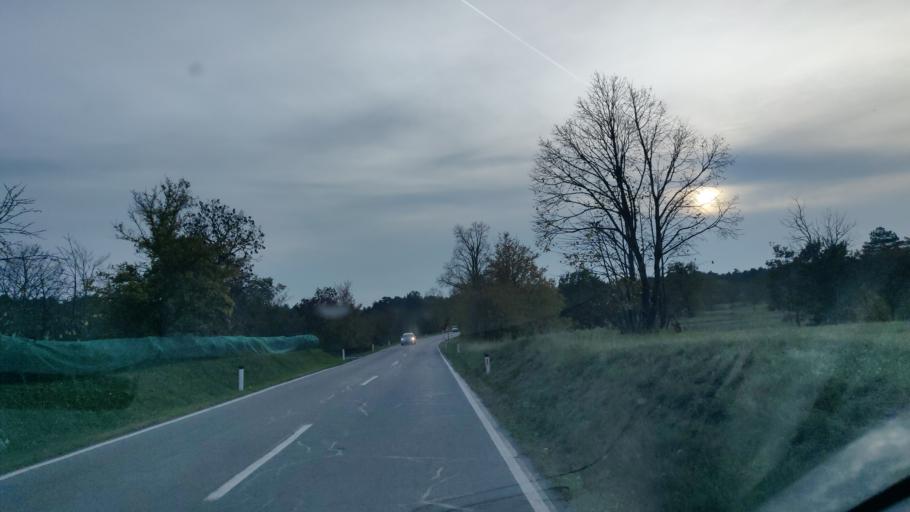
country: SI
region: Ajdovscina
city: Lokavec
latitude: 45.8091
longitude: 13.8474
